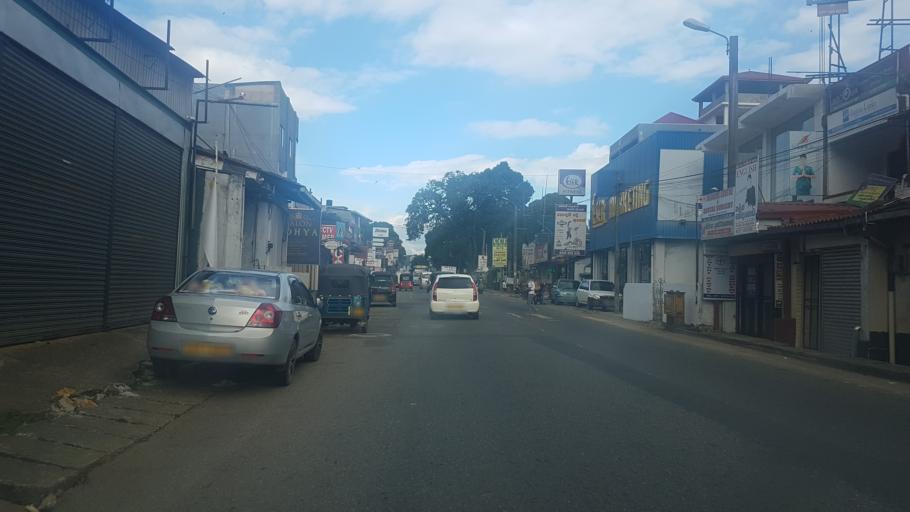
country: LK
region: Central
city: Kandy
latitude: 7.2796
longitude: 80.6184
